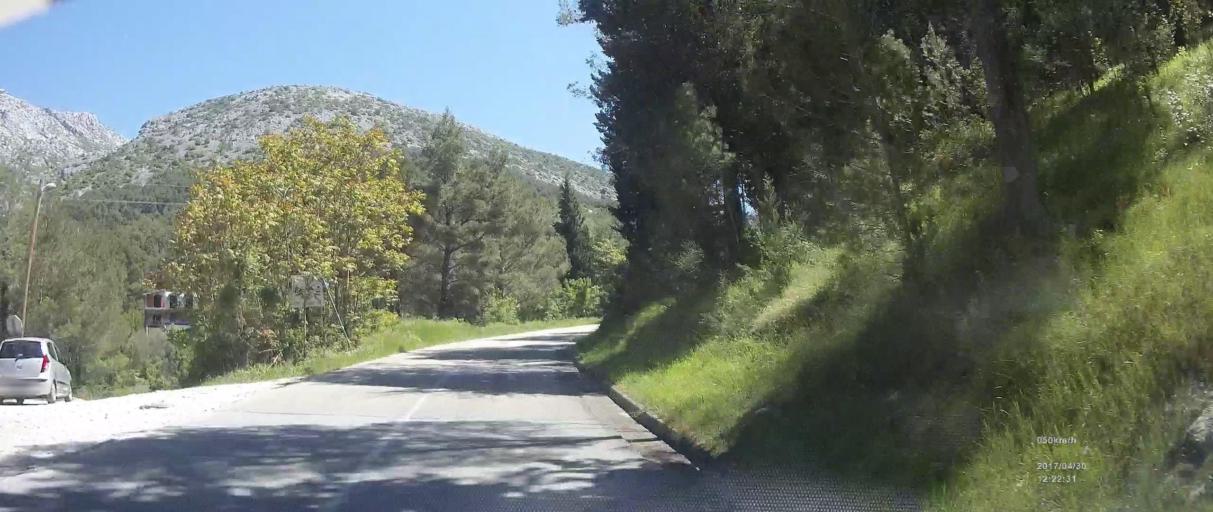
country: HR
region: Splitsko-Dalmatinska
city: Zrnovnica
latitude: 43.5202
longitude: 16.5709
